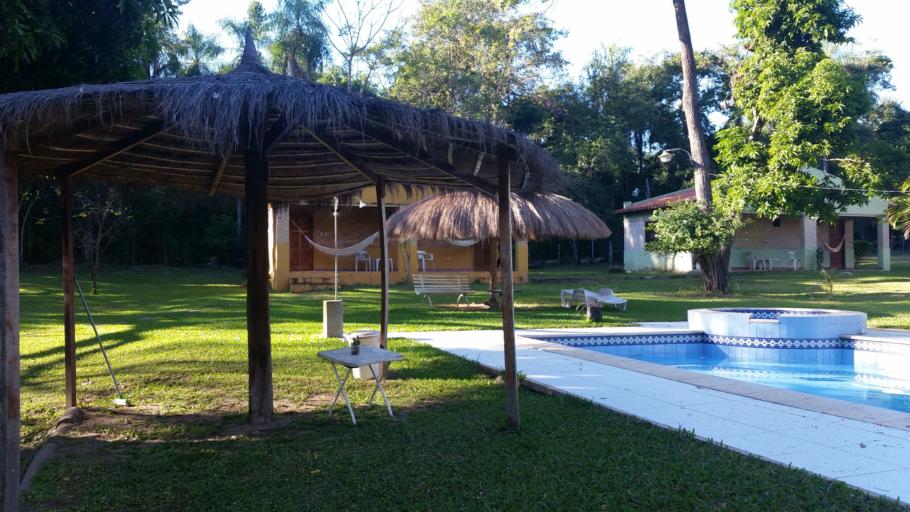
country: PY
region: Cordillera
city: Arroyos y Esteros
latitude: -24.9981
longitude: -57.1821
